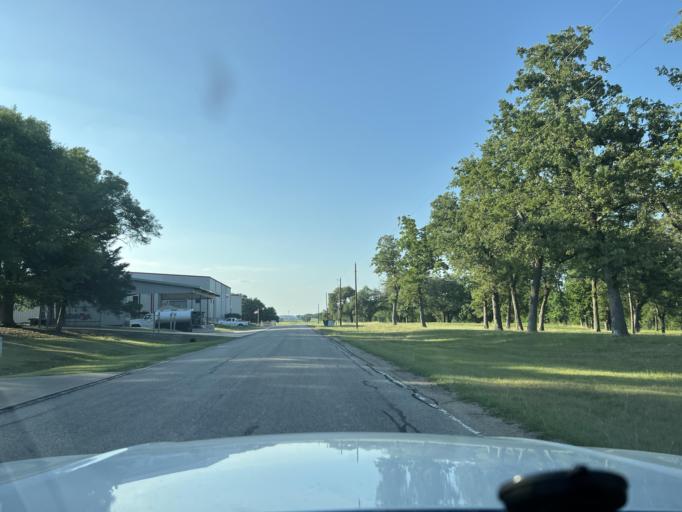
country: US
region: Texas
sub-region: Washington County
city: Brenham
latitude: 30.2118
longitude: -96.3708
